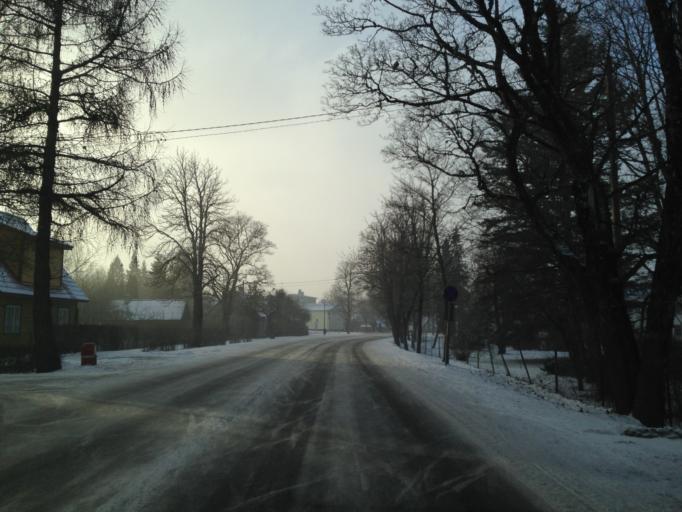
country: EE
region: Raplamaa
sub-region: Maerjamaa vald
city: Marjamaa
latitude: 58.9061
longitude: 24.4296
